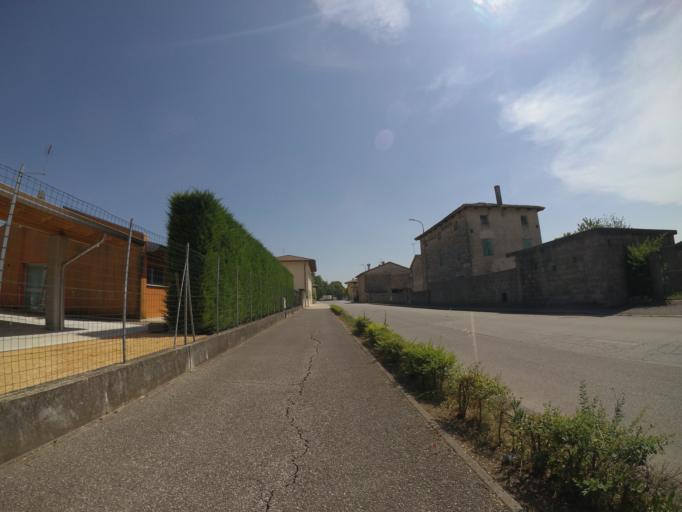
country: IT
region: Friuli Venezia Giulia
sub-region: Provincia di Udine
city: Camino al Tagliamento
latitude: 45.9287
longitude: 12.9448
